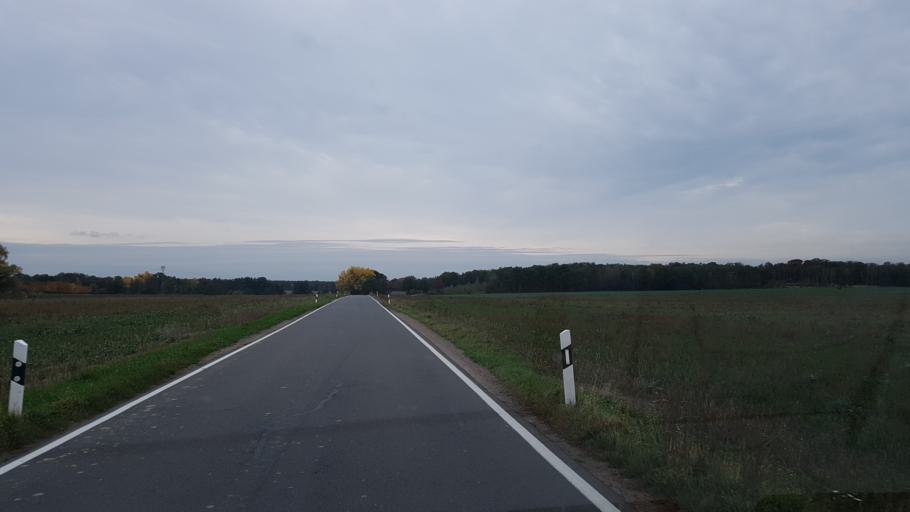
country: DE
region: Saxony
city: Falkenhain
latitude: 51.3801
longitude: 12.9166
